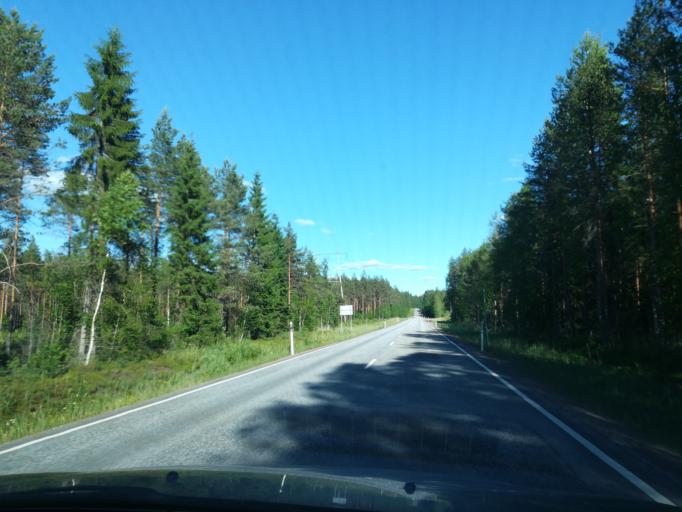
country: FI
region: South Karelia
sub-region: Imatra
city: Ruokolahti
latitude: 61.4035
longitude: 28.5815
